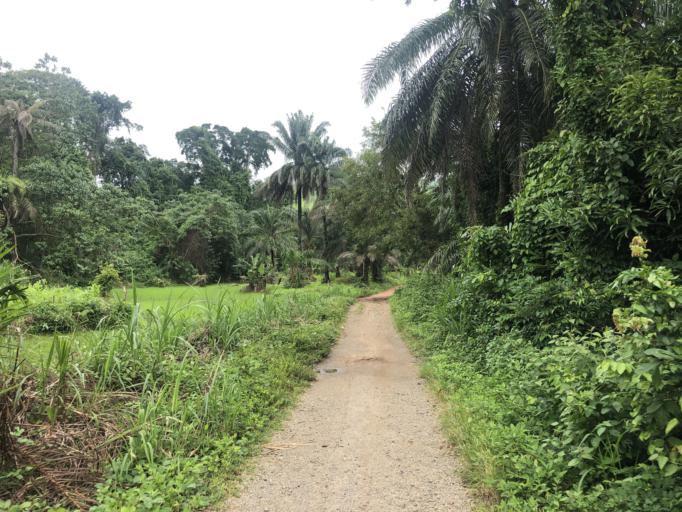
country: SL
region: Northern Province
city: Bumbuna
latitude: 8.9951
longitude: -11.7555
